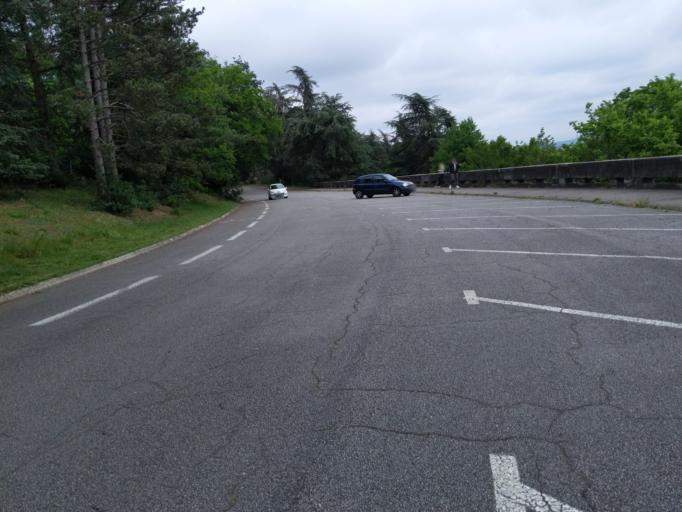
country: FR
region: Rhone-Alpes
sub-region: Departement du Rhone
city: Bron
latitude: 45.7278
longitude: 4.8918
